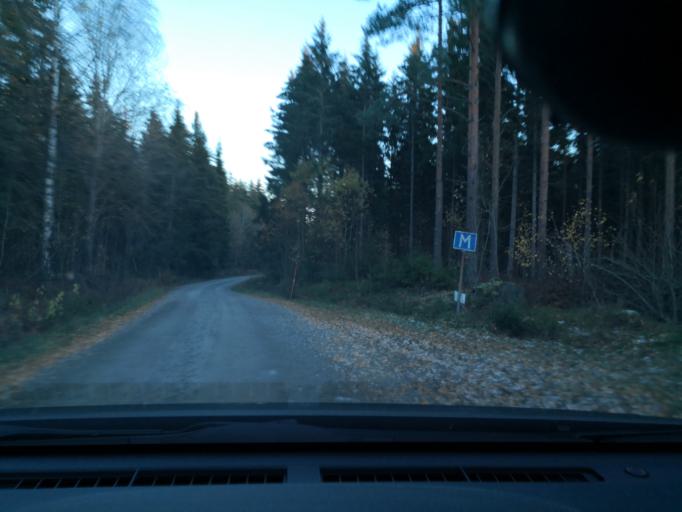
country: SE
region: Vaestmanland
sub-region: Vasteras
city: Tillberga
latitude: 59.7641
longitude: 16.6128
